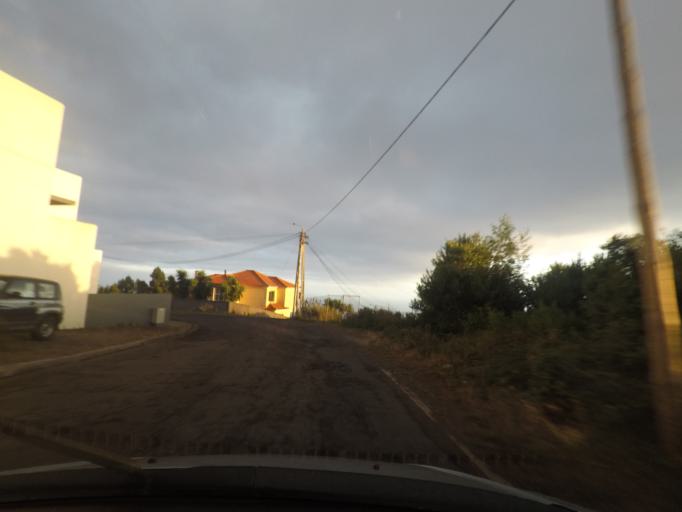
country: PT
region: Madeira
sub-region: Santa Cruz
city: Camacha
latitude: 32.6664
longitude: -16.8425
